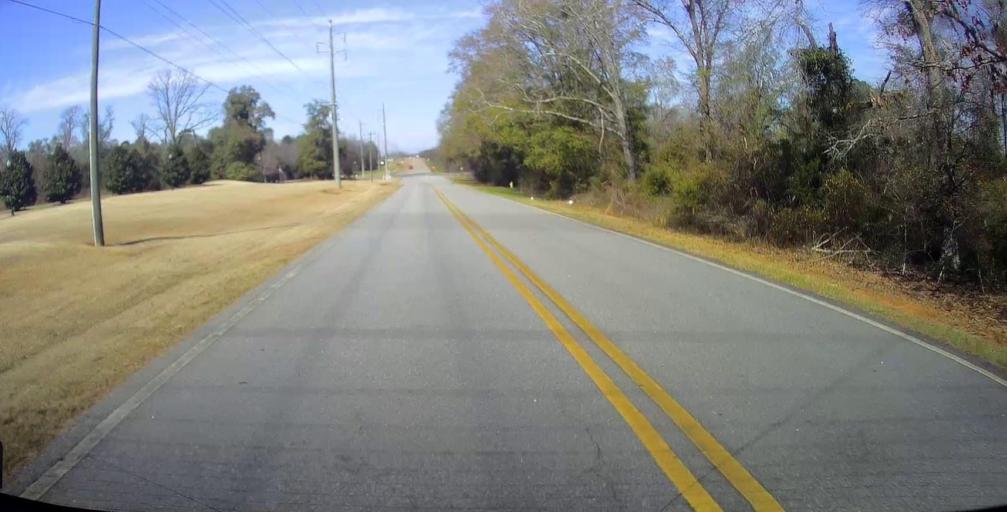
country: US
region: Georgia
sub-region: Houston County
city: Perry
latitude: 32.4787
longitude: -83.7589
